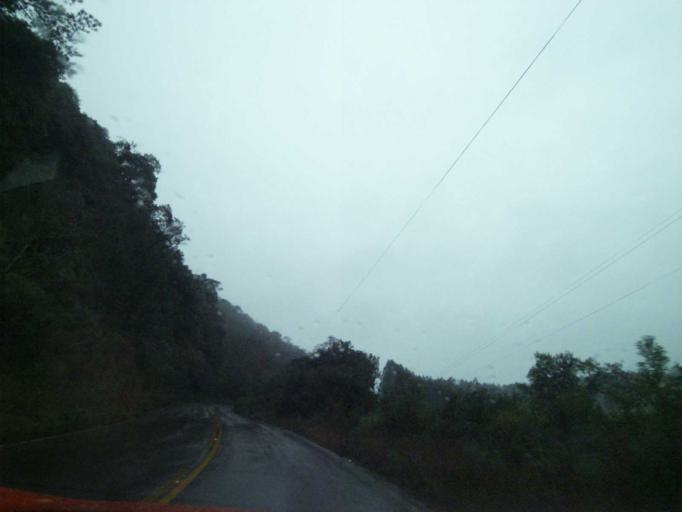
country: BR
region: Santa Catarina
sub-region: Anitapolis
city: Anitapolis
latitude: -27.8464
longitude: -49.0541
